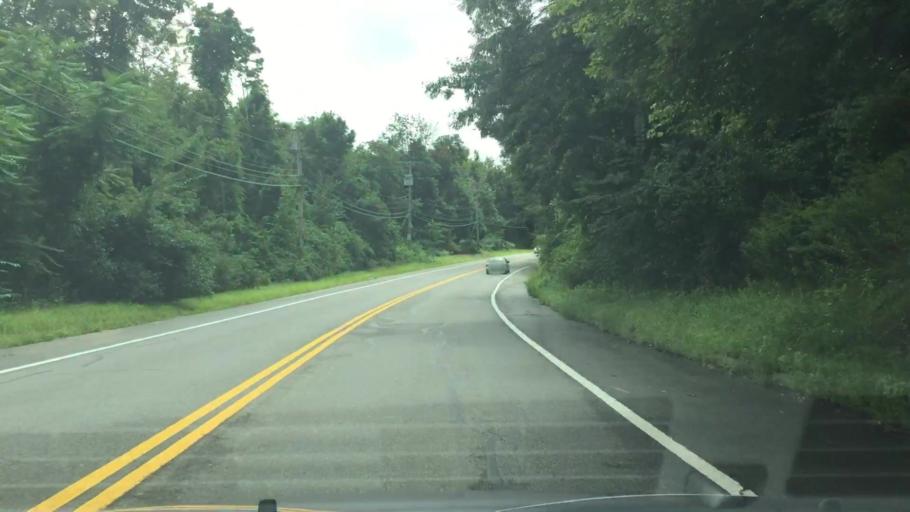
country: US
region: Massachusetts
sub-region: Essex County
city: North Andover
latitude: 42.7104
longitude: -71.1179
